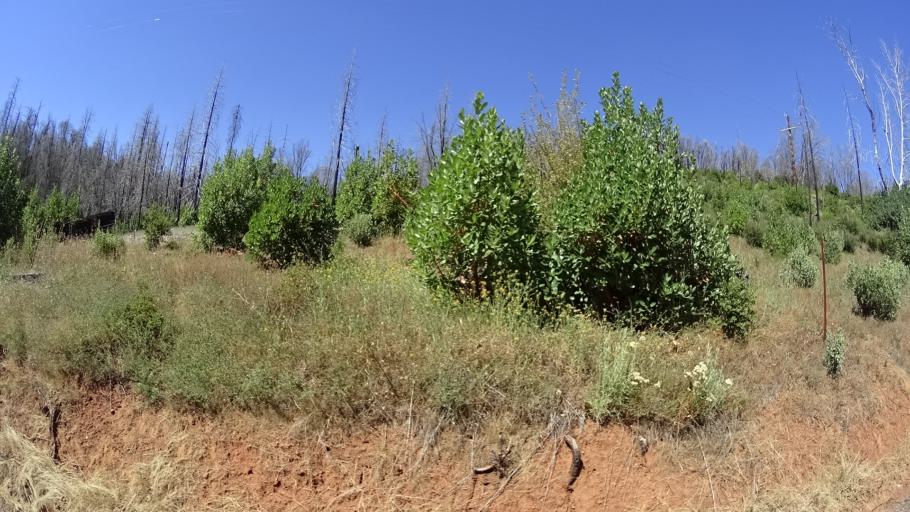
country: US
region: California
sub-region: Calaveras County
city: Mountain Ranch
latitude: 38.2833
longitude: -120.5667
